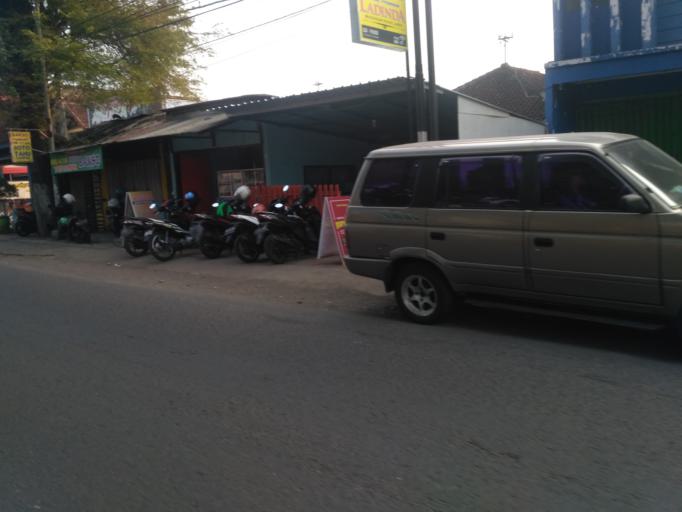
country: ID
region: East Java
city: Kebonsari
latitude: -8.0135
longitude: 112.6204
